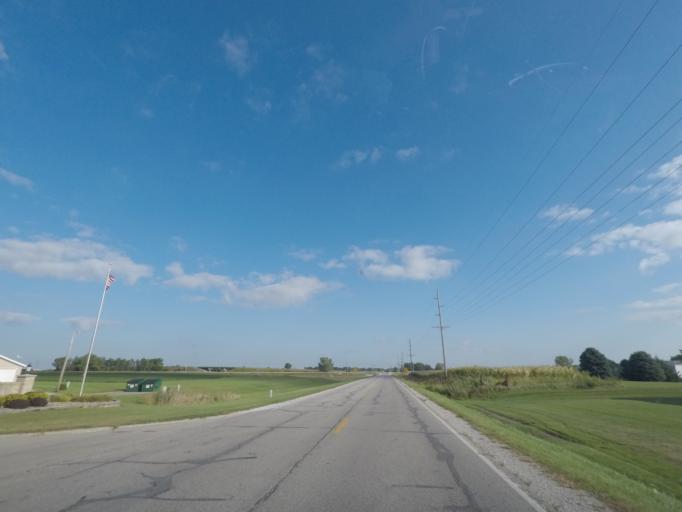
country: US
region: Iowa
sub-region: Story County
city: Nevada
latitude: 42.0020
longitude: -93.4628
